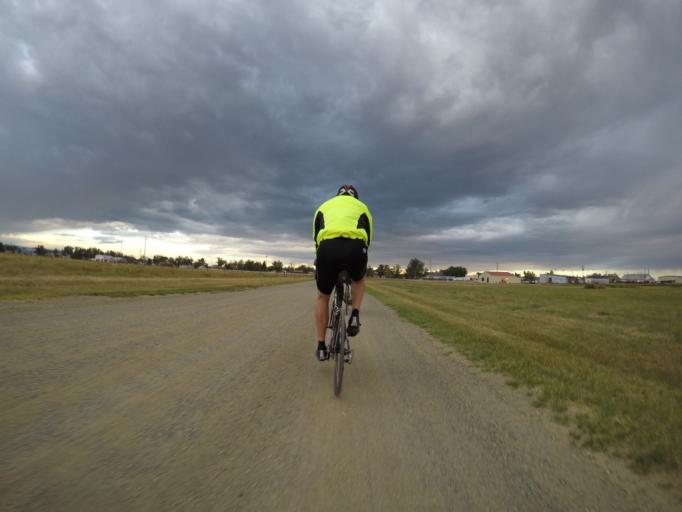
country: US
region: Wyoming
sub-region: Albany County
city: Laramie
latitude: 41.7425
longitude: -105.9734
